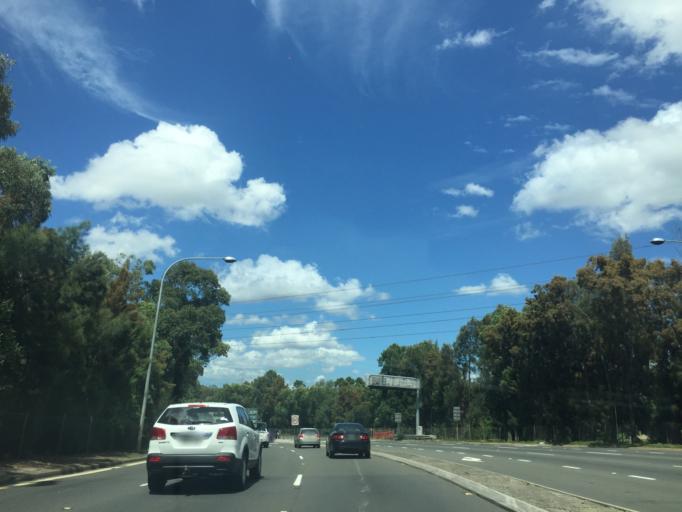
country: AU
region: New South Wales
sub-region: Strathfield
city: Homebush
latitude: -33.8683
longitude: 151.0642
